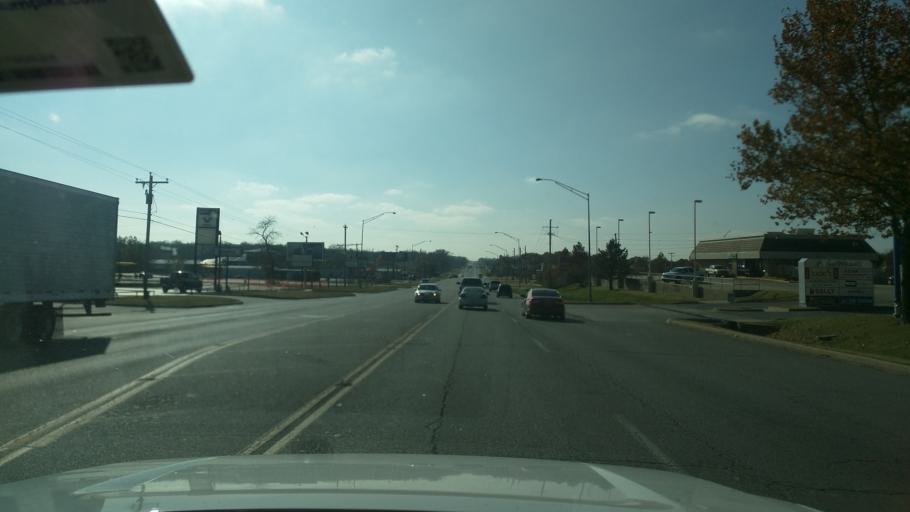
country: US
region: Oklahoma
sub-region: Washington County
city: Bartlesville
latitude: 36.7132
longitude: -95.9352
